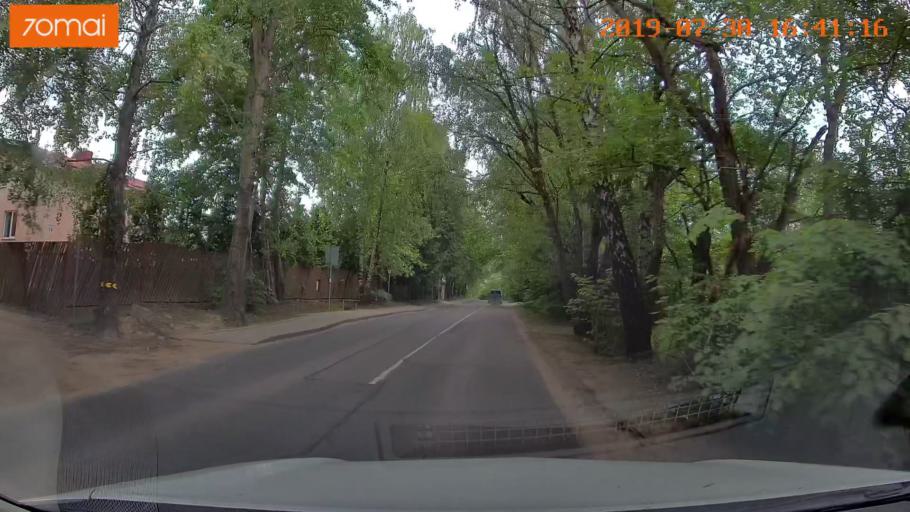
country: LT
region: Vilnius County
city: Rasos
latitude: 54.7101
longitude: 25.3572
